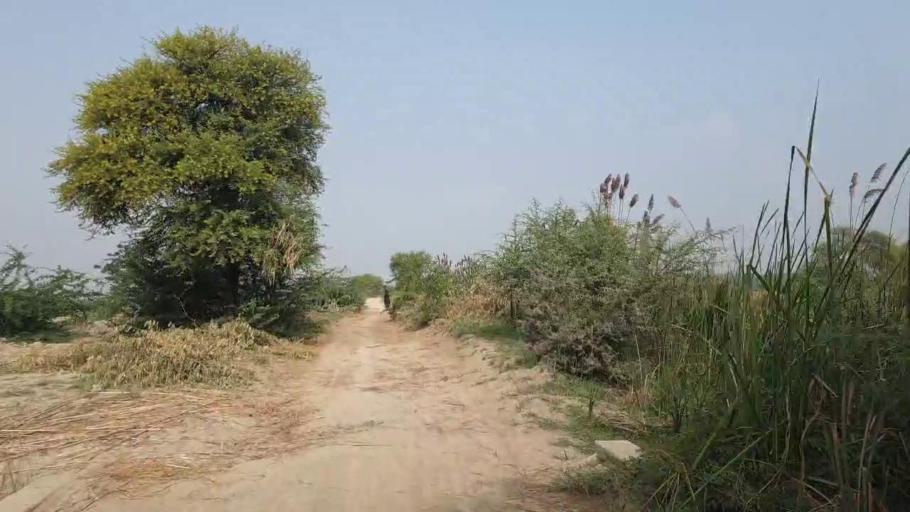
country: PK
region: Sindh
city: Kario
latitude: 24.7716
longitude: 68.5229
